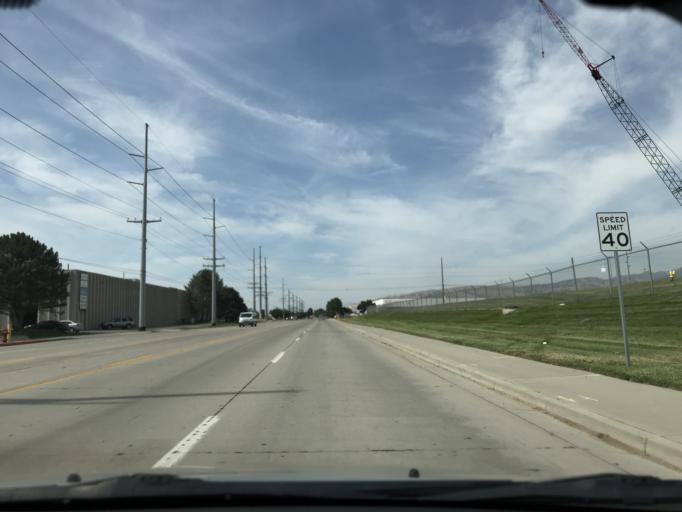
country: US
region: Utah
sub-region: Salt Lake County
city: Centerfield
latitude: 40.7064
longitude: -111.9169
